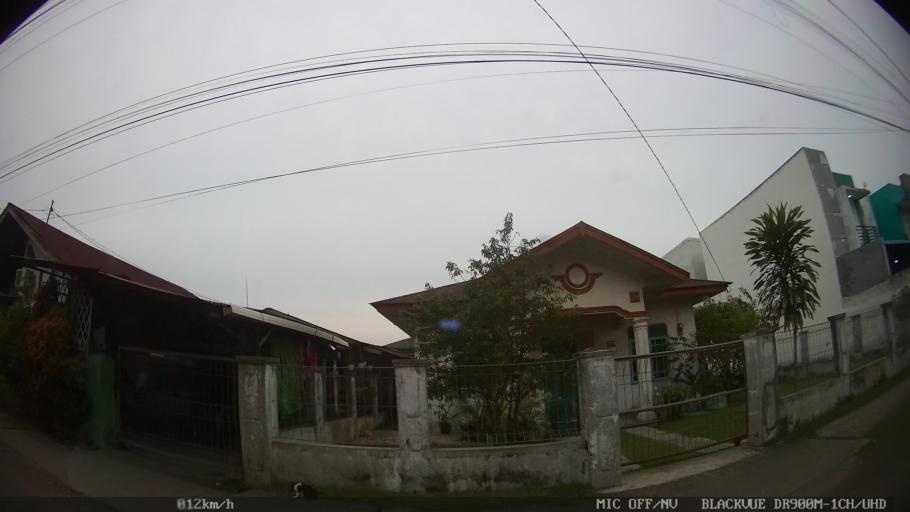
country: ID
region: North Sumatra
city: Deli Tua
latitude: 3.5430
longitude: 98.7113
